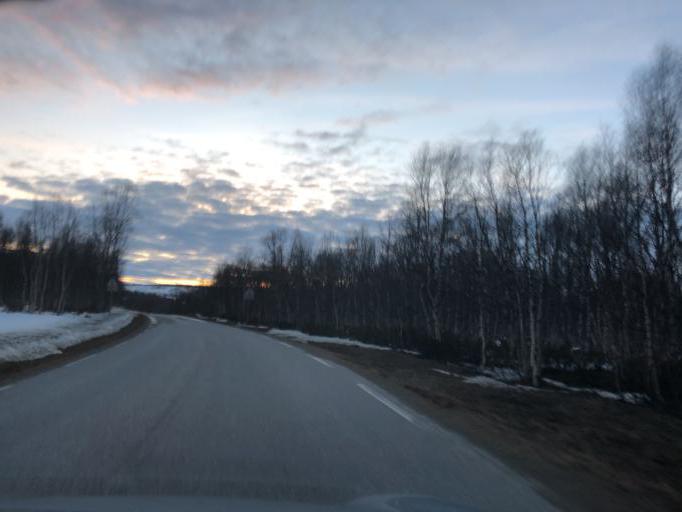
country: NO
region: Sor-Trondelag
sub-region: Tydal
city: Aas
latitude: 62.6767
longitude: 11.8616
